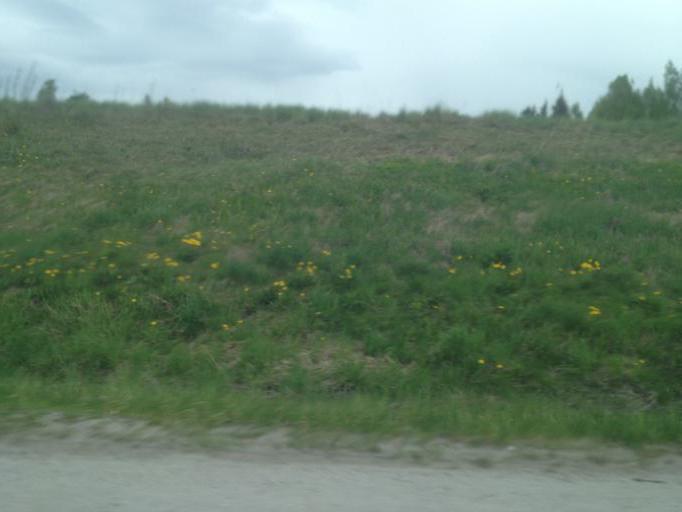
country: FI
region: Uusimaa
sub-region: Helsinki
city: Kilo
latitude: 60.3322
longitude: 24.8211
